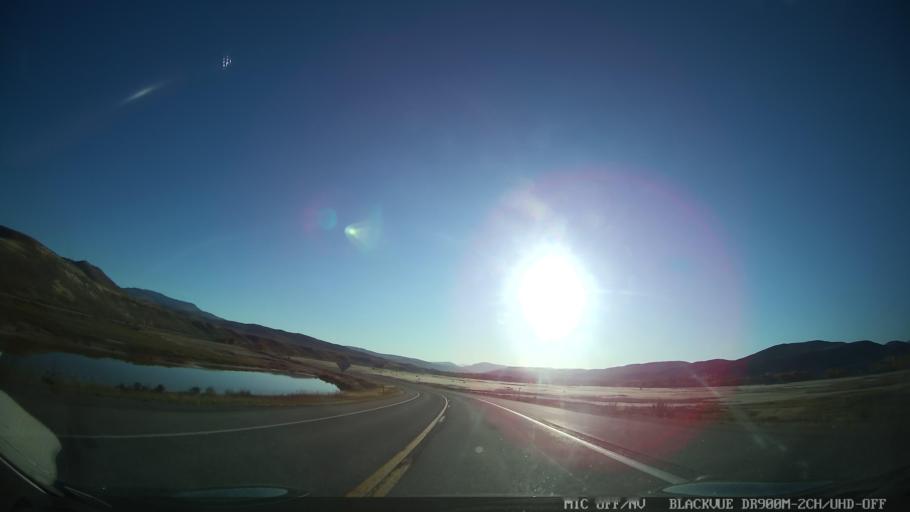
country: US
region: Colorado
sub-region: Grand County
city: Kremmling
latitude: 40.0644
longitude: -106.2821
